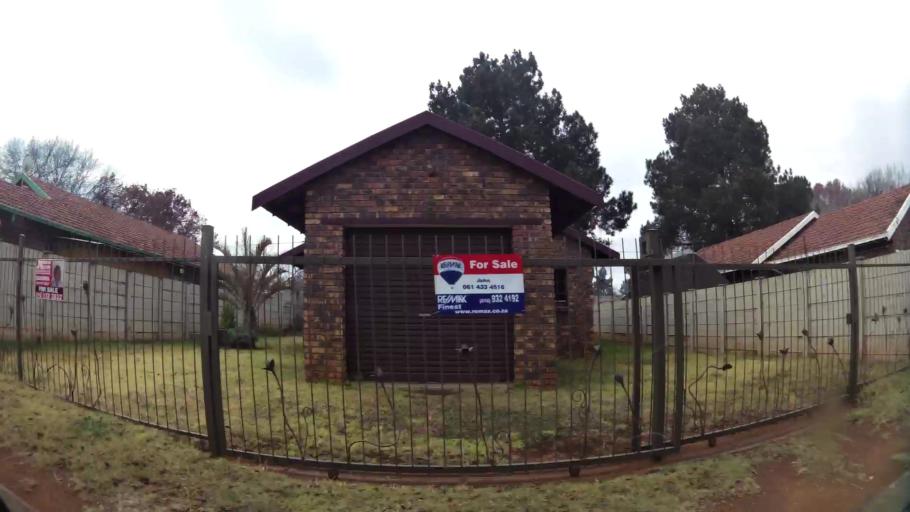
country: ZA
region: Gauteng
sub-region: Sedibeng District Municipality
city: Vanderbijlpark
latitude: -26.7014
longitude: 27.8433
